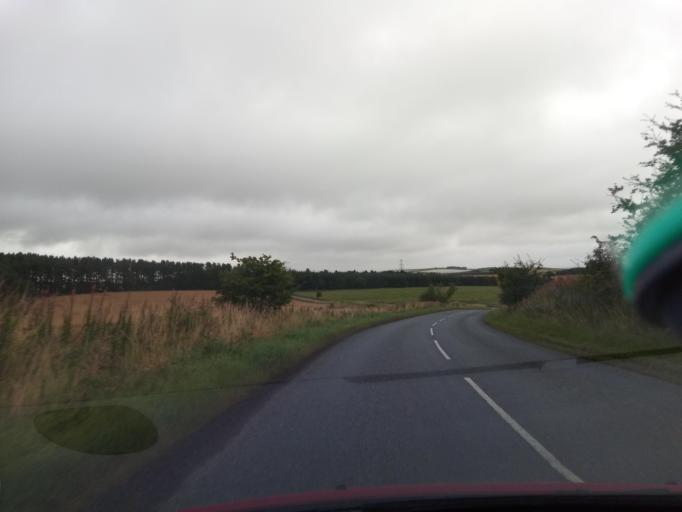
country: GB
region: Scotland
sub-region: The Scottish Borders
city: Earlston
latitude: 55.6600
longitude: -2.5526
